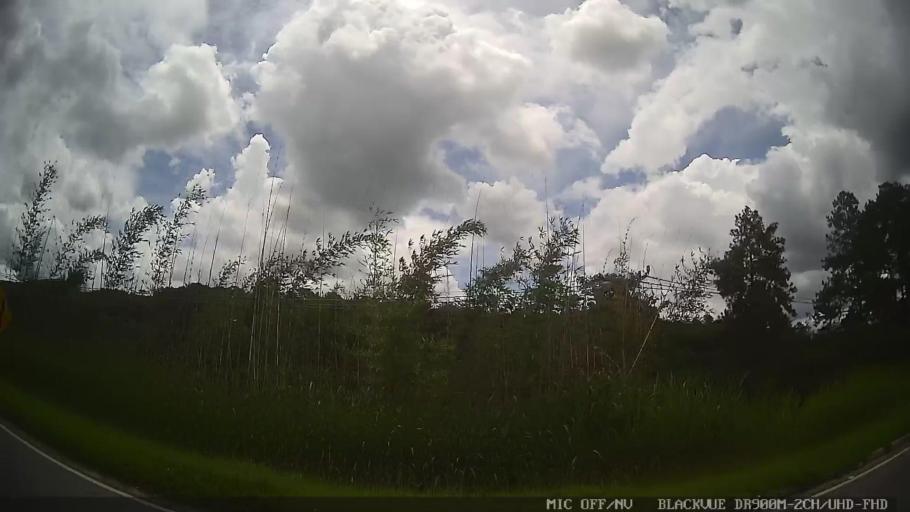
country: BR
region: Sao Paulo
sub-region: Suzano
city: Suzano
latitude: -23.6203
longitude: -46.3182
